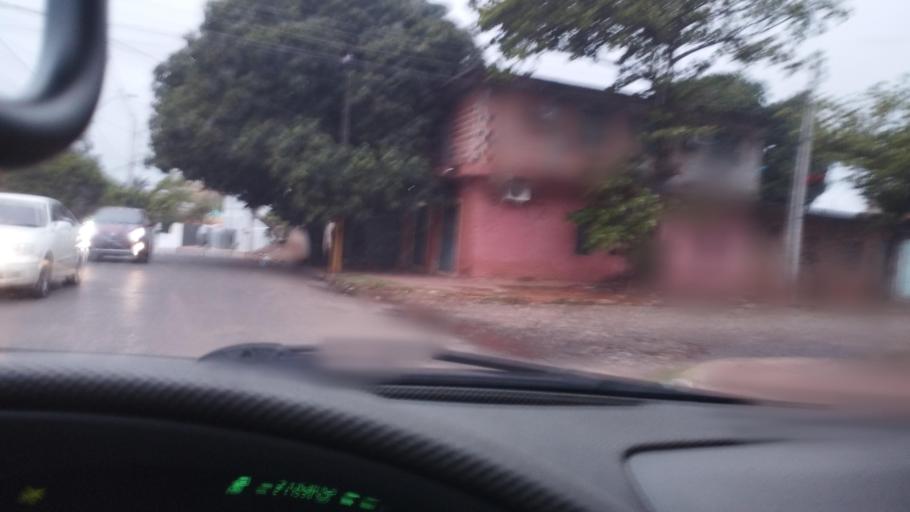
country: PY
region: Central
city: Fernando de la Mora
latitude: -25.3048
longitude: -57.5328
